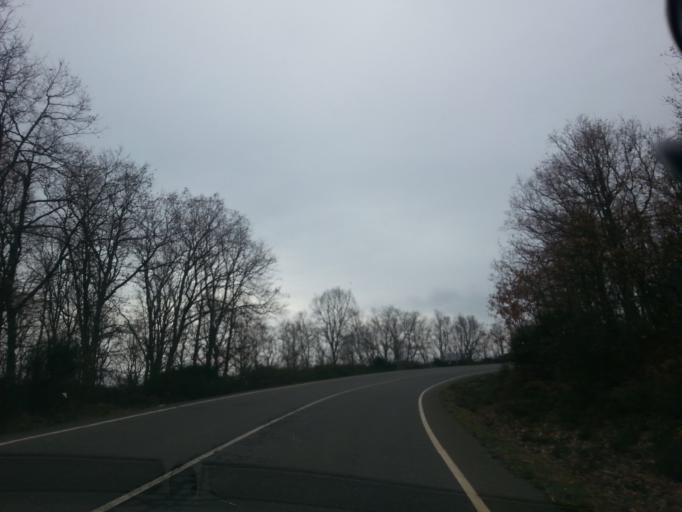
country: ES
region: Castille and Leon
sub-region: Provincia de Salamanca
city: Madronal
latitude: 40.4696
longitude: -6.0663
